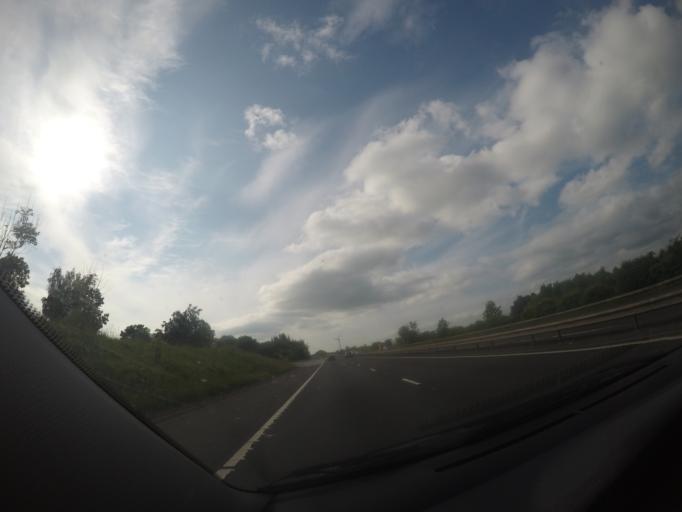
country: GB
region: Scotland
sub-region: South Lanarkshire
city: Lesmahagow
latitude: 55.6523
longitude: -3.8950
